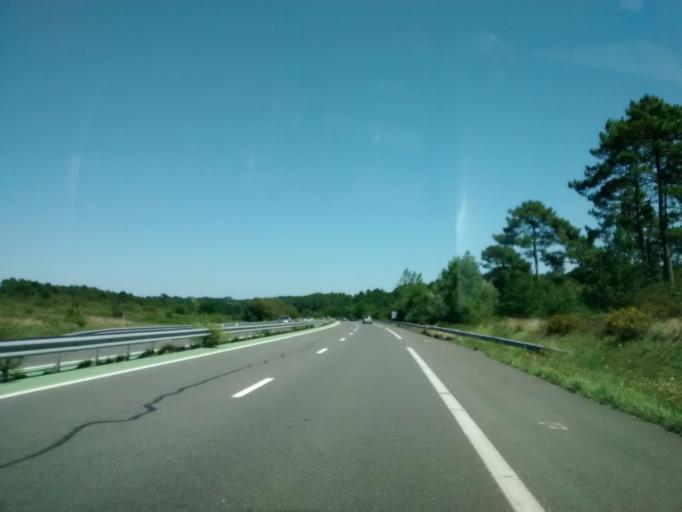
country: FR
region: Aquitaine
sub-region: Departement de la Dordogne
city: Montpon-Menesterol
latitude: 44.9855
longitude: 0.1850
